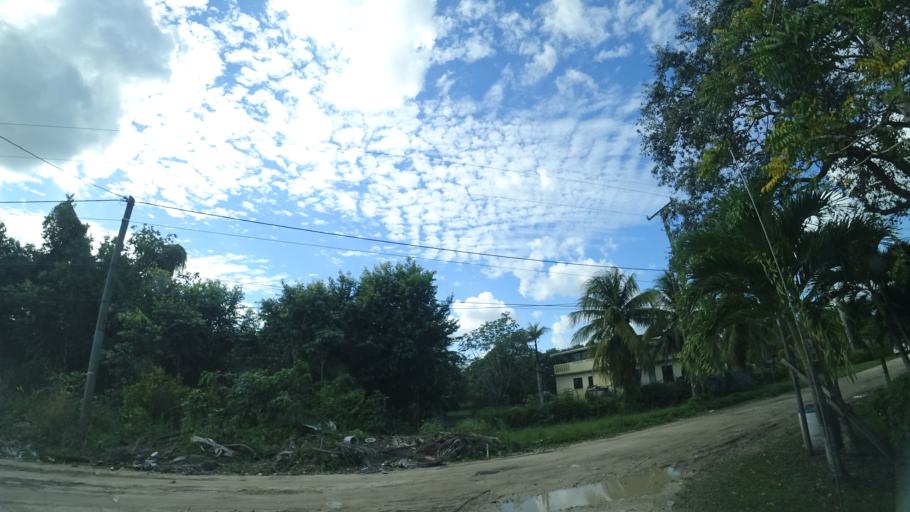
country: BZ
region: Belize
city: Belize City
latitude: 17.5647
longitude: -88.4085
